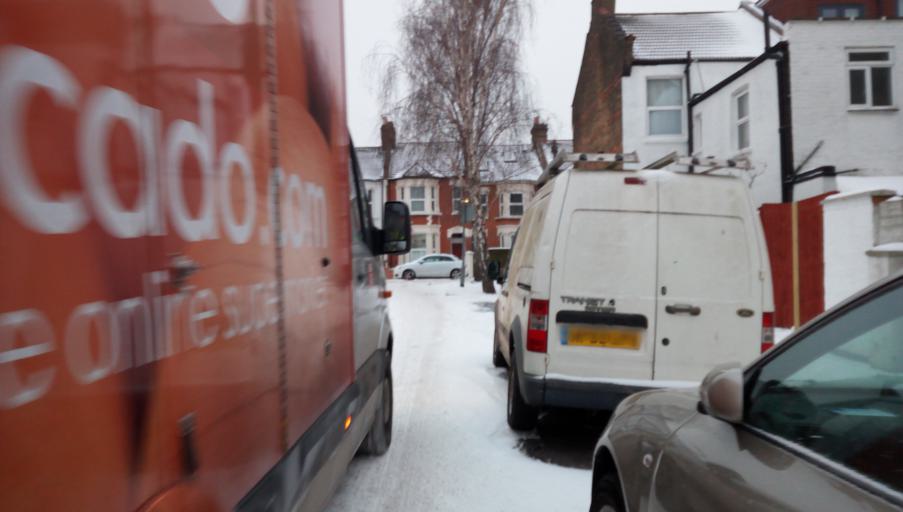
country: GB
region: England
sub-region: Greater London
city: Hammersmith
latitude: 51.5323
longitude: -0.2264
